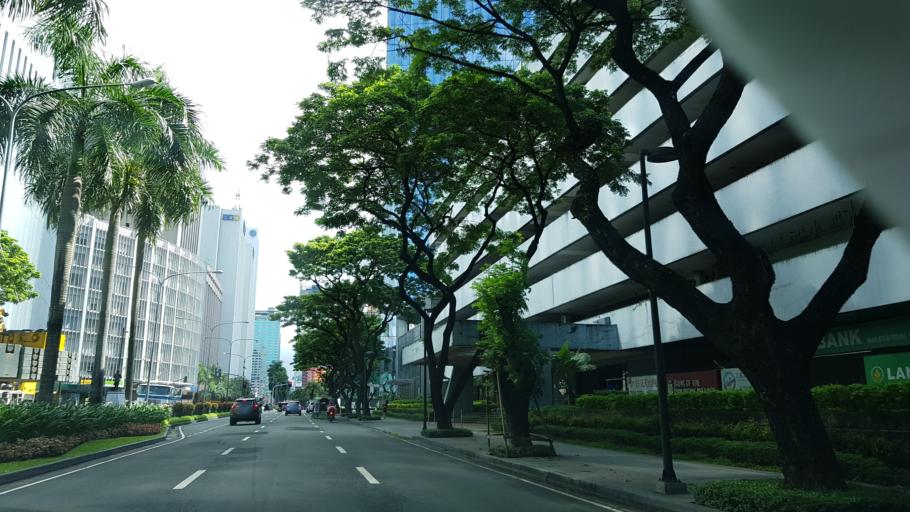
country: PH
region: Metro Manila
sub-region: Makati City
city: Makati City
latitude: 14.5568
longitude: 121.0257
